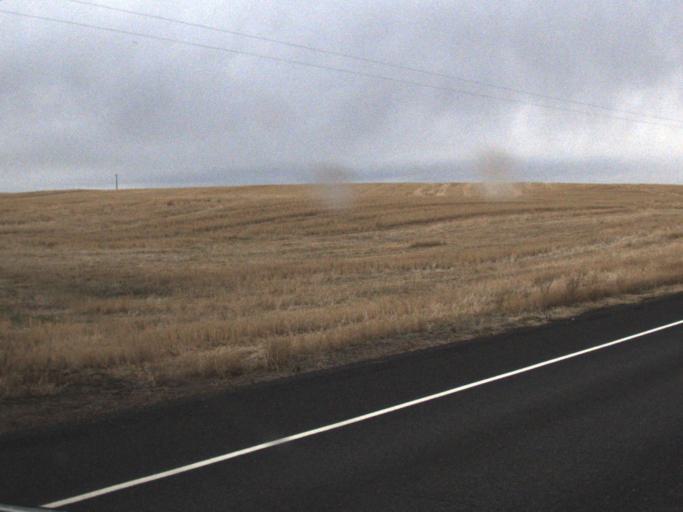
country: US
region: Washington
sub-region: Garfield County
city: Pomeroy
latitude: 46.8111
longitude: -117.7987
